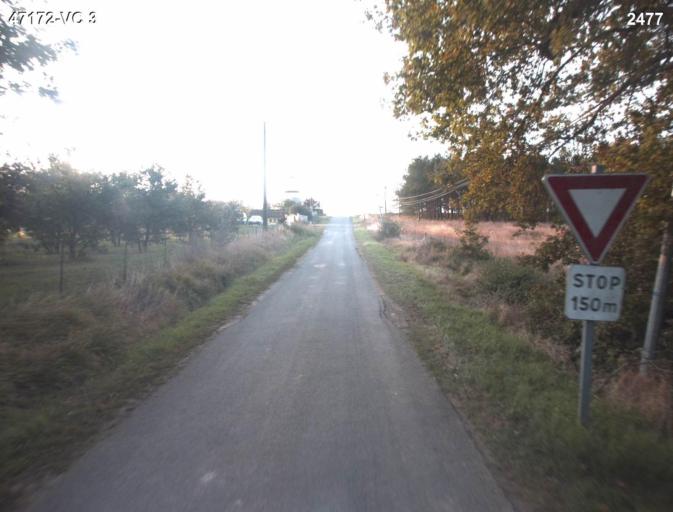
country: FR
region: Aquitaine
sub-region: Departement du Lot-et-Garonne
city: Sainte-Colombe-en-Bruilhois
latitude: 44.1490
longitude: 0.4938
